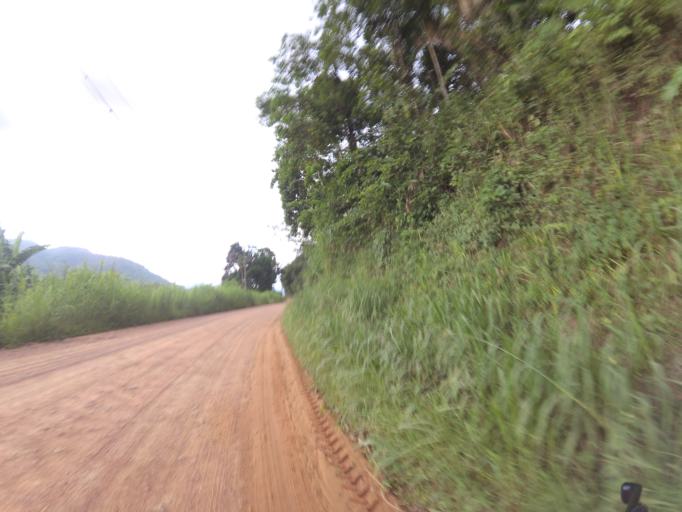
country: BR
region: Santa Catarina
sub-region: Pomerode
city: Pomerode
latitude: -26.7612
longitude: -49.1658
